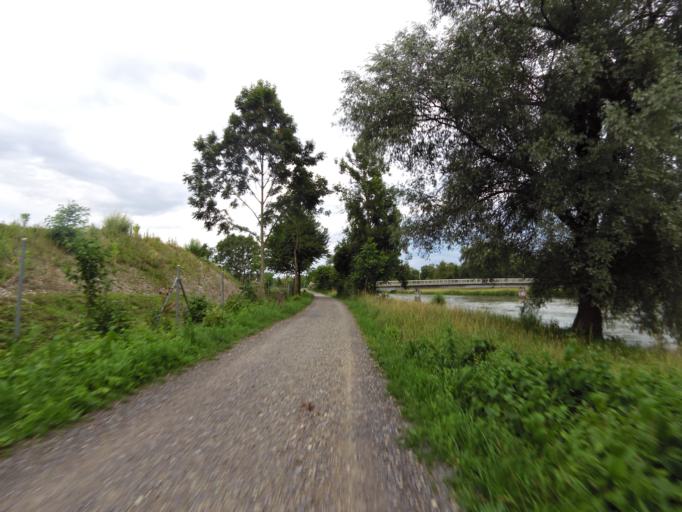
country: CH
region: Zurich
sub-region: Bezirk Dietikon
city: Oberengstringen / Rauchacher
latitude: 47.4055
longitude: 8.4580
